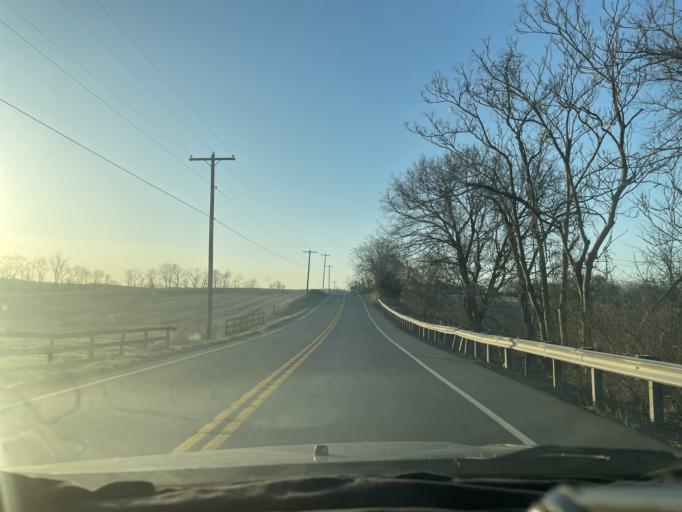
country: US
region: Maryland
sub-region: Frederick County
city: Adamstown
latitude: 39.2507
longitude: -77.4449
